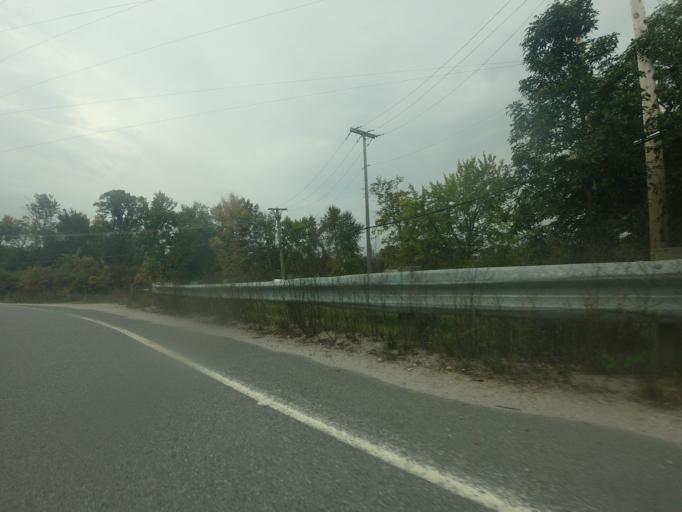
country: CA
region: Quebec
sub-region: Outaouais
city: Maniwaki
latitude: 46.0903
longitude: -76.0448
